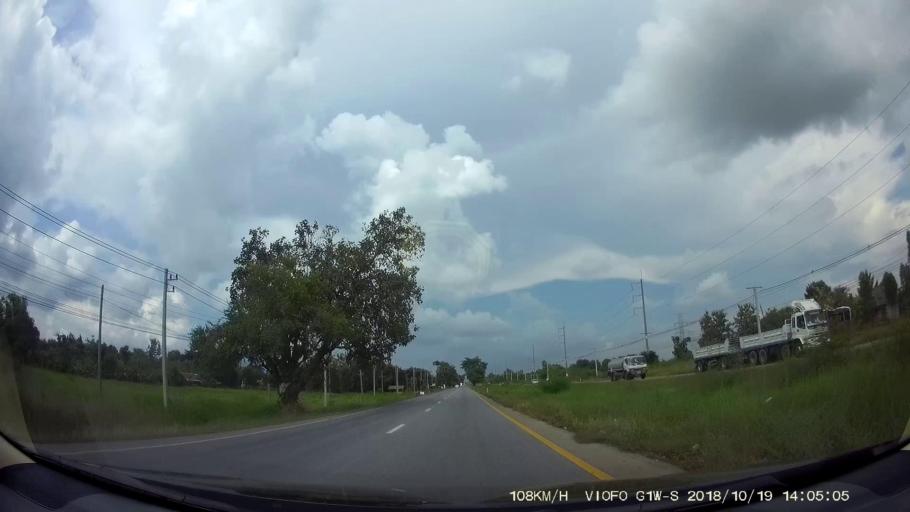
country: TH
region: Chaiyaphum
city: Chaiyaphum
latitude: 15.8710
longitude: 102.0889
